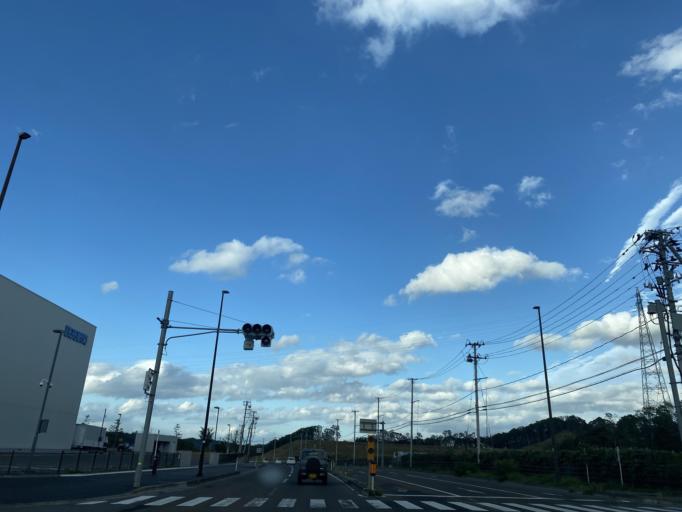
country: JP
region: Miyagi
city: Tomiya
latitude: 38.3695
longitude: 140.8548
